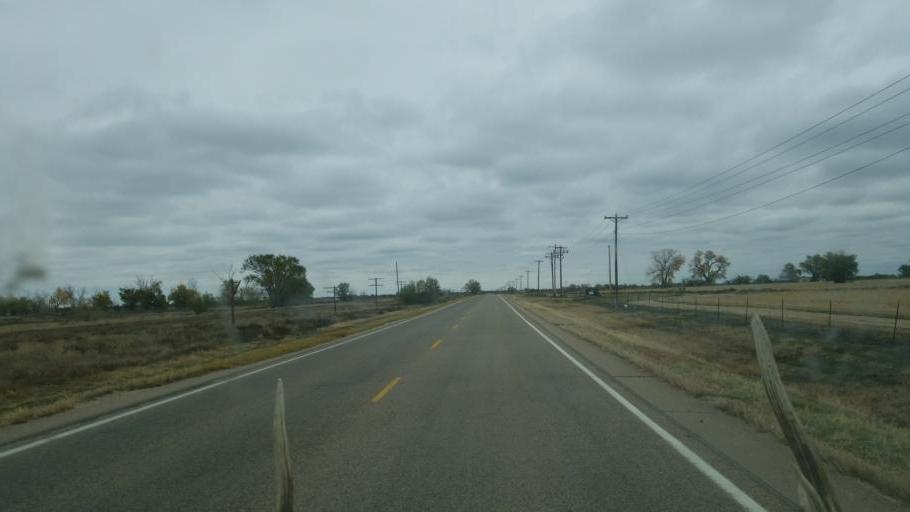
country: US
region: Colorado
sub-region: Crowley County
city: Ordway
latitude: 38.1954
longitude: -103.8450
